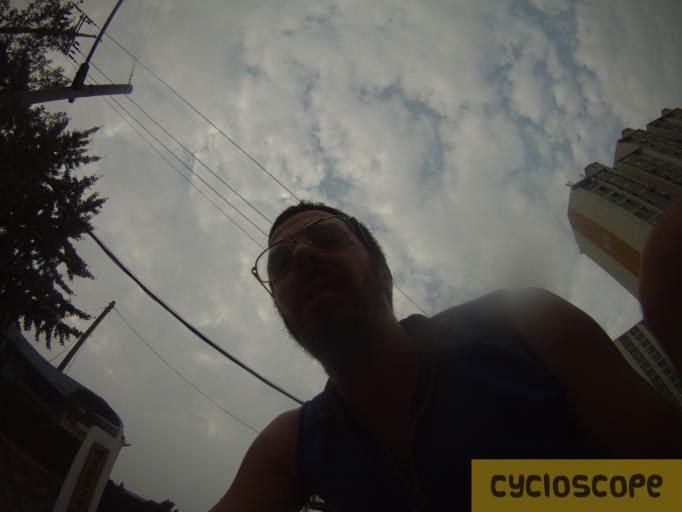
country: KR
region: Gyeonggi-do
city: Suwon-si
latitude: 37.2403
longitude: 126.9623
